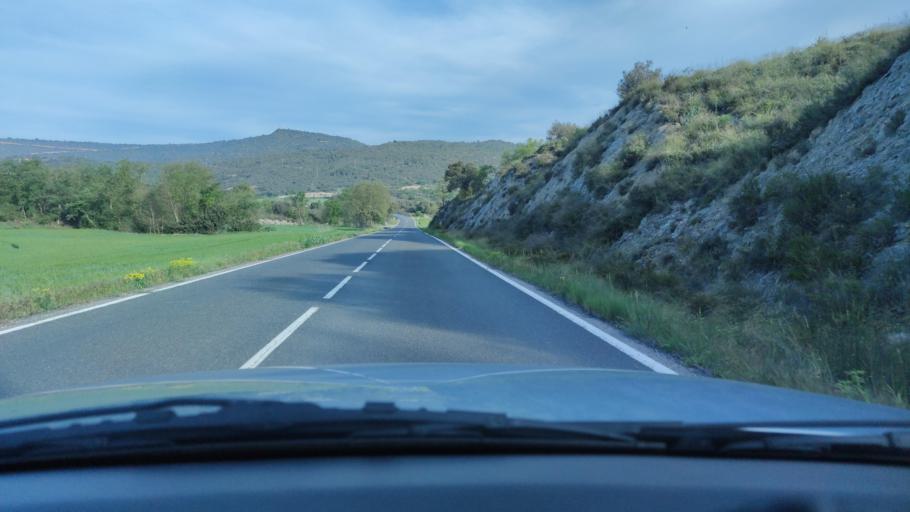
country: ES
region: Catalonia
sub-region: Provincia de Lleida
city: Ponts
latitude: 41.8928
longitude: 1.1776
